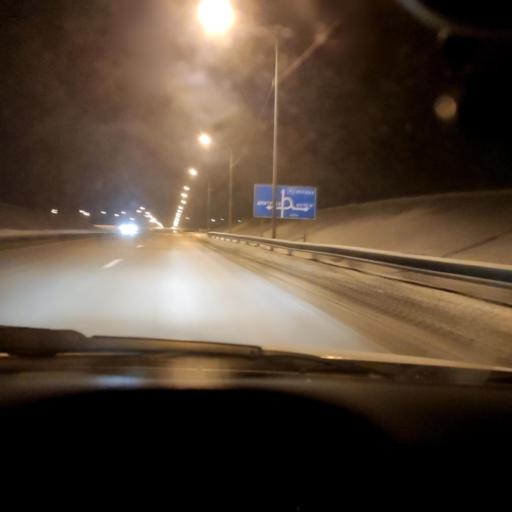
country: RU
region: Kursk
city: Fatezh
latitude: 52.0938
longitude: 35.8199
